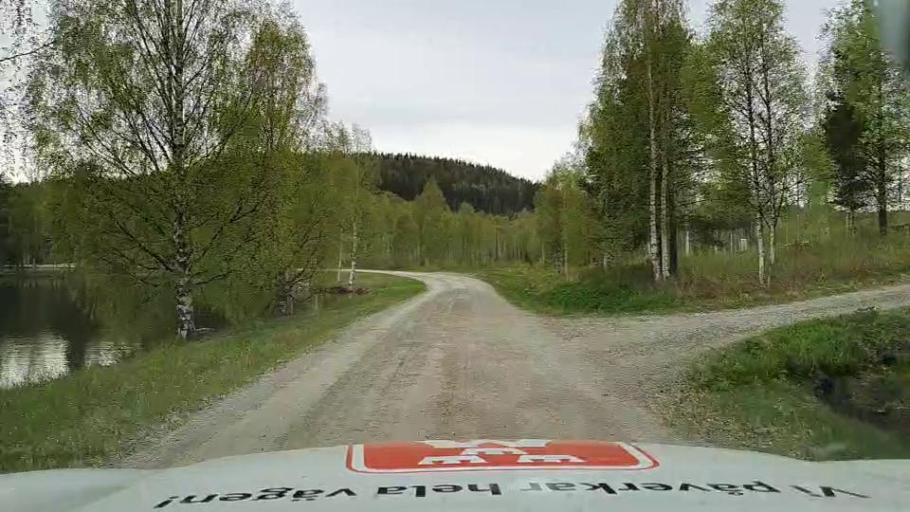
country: SE
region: Jaemtland
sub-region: Bergs Kommun
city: Hoverberg
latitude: 62.6891
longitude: 14.7802
